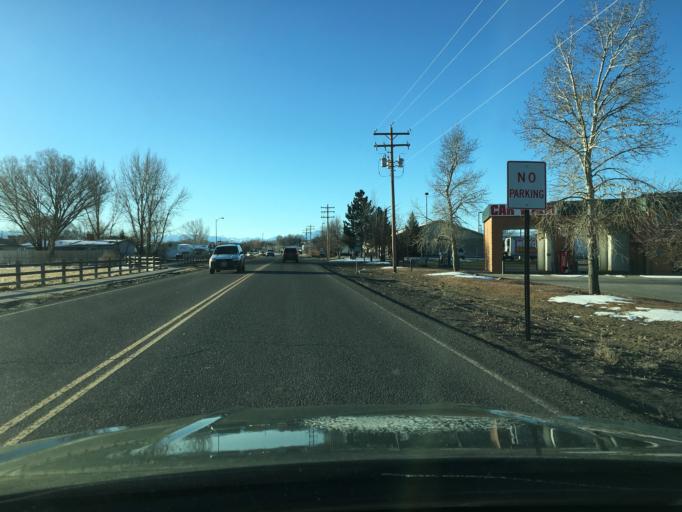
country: US
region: Colorado
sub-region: Montrose County
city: Montrose
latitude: 38.4533
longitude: -107.8639
